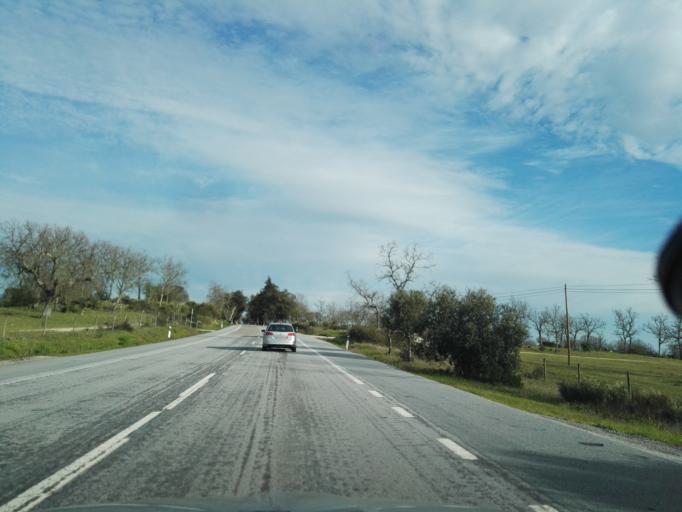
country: PT
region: Portalegre
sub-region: Portalegre
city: Alagoa
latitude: 39.3808
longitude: -7.5848
